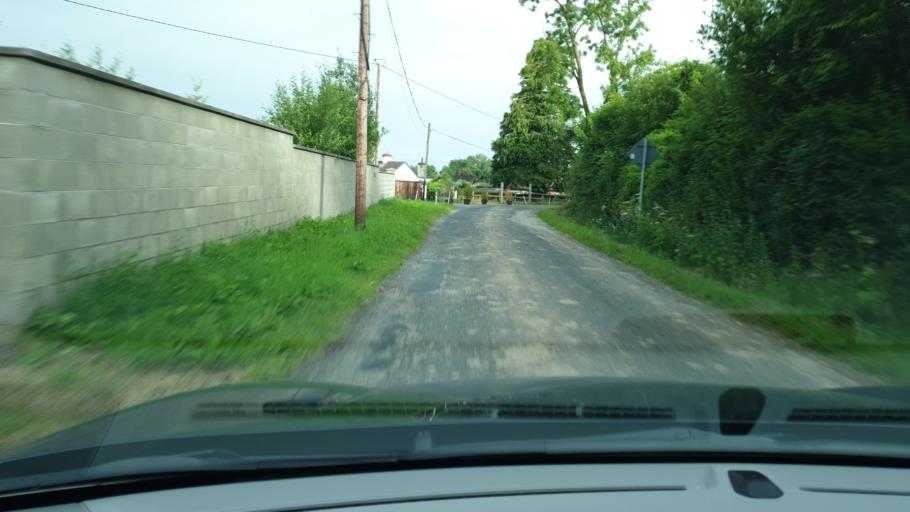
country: IE
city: Confey
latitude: 53.4082
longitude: -6.5115
